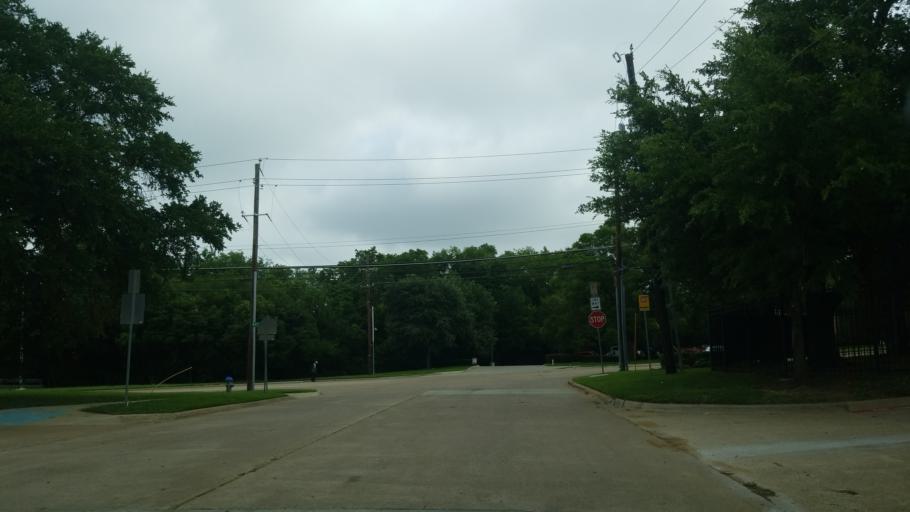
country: US
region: Texas
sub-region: Dallas County
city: University Park
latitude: 32.8365
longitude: -96.8689
